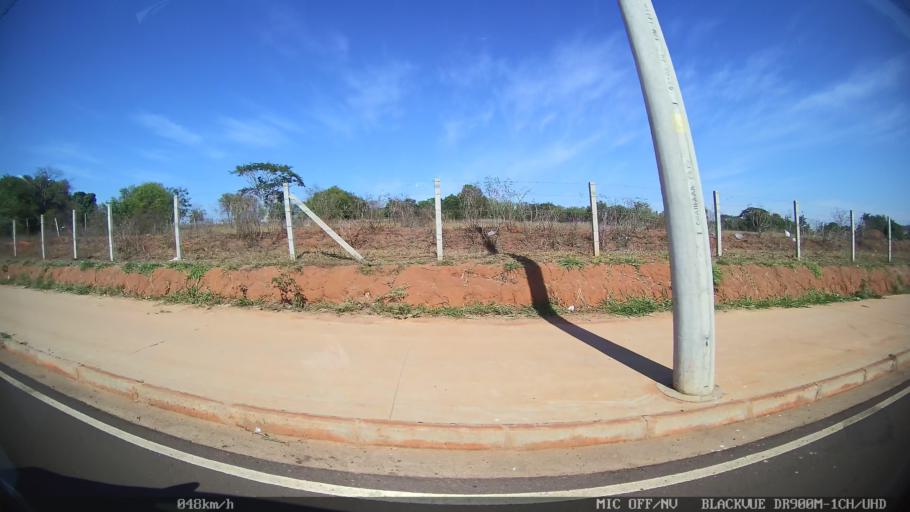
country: BR
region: Sao Paulo
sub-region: Sao Jose Do Rio Preto
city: Sao Jose do Rio Preto
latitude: -20.7611
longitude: -49.3705
